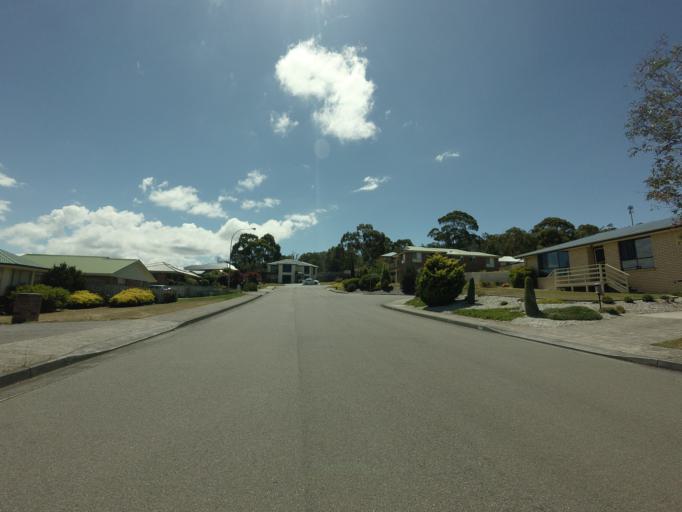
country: AU
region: Tasmania
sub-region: Clarence
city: Rokeby
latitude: -42.8986
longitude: 147.4565
